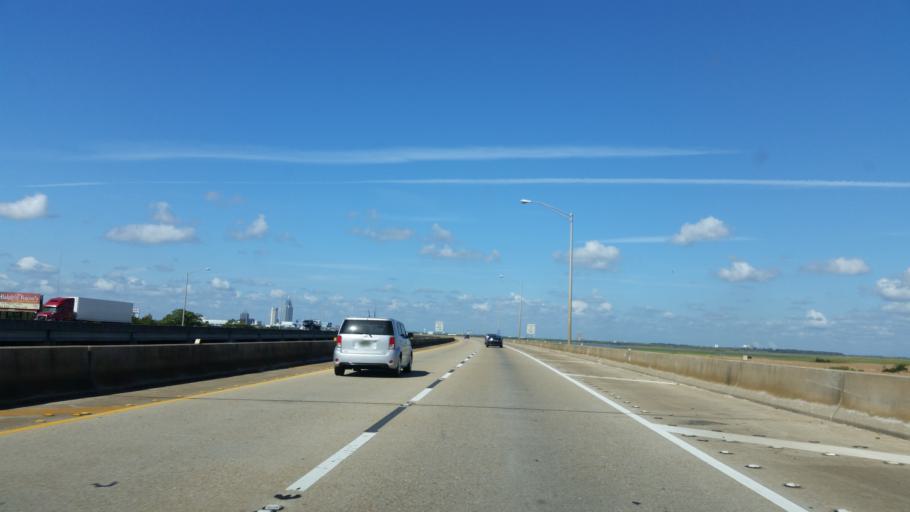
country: US
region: Alabama
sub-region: Mobile County
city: Mobile
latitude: 30.6821
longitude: -87.9929
